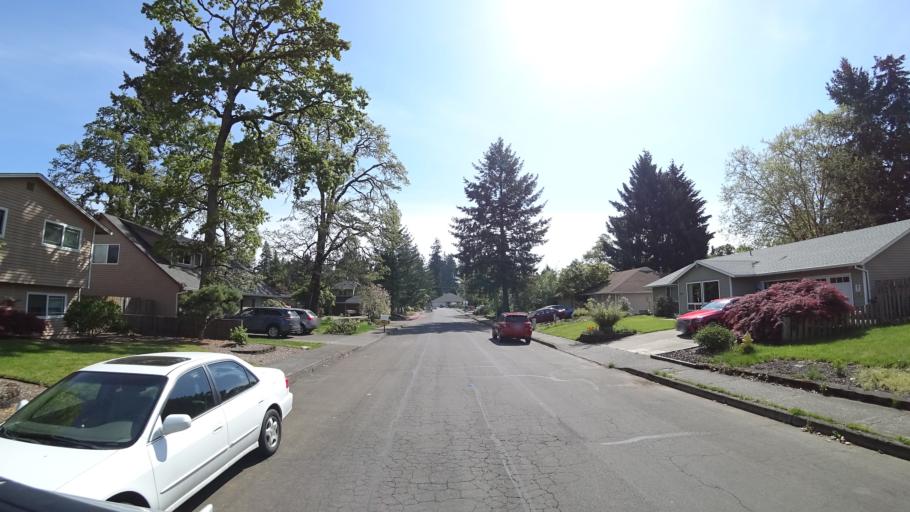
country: US
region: Oregon
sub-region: Washington County
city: Hillsboro
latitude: 45.5232
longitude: -122.9402
